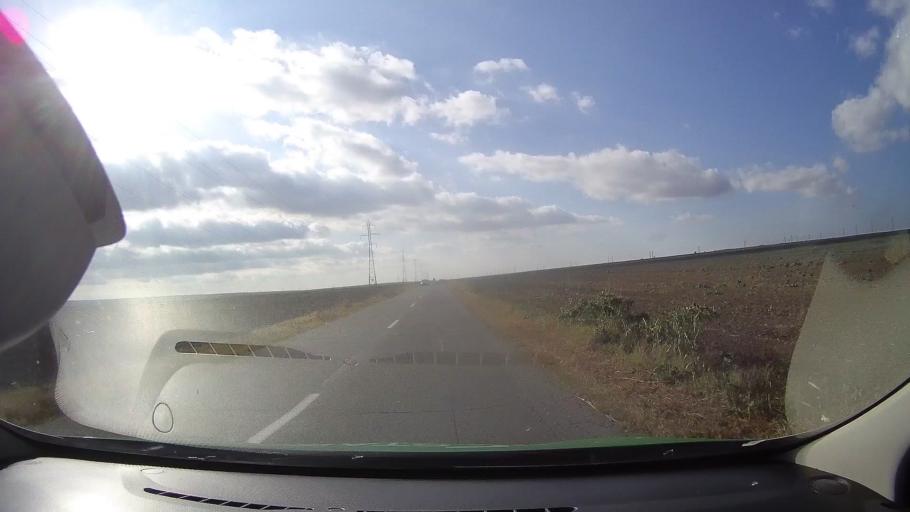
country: RO
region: Constanta
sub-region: Comuna Sacele
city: Sacele
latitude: 44.5098
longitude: 28.6765
